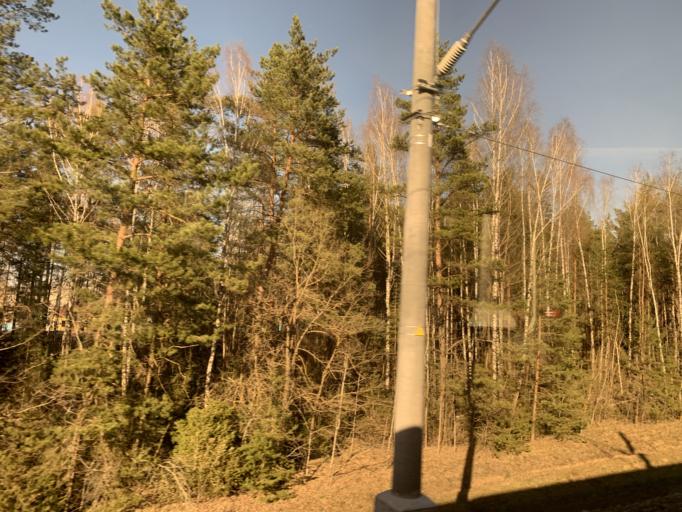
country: BY
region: Grodnenskaya
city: Smarhon'
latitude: 54.4374
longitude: 26.5116
